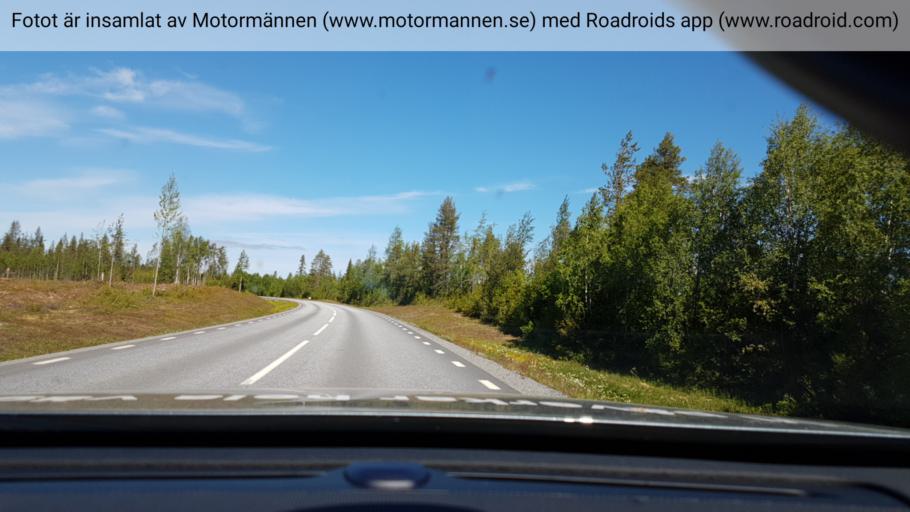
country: SE
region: Vaesterbotten
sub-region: Vilhelmina Kommun
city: Vilhelmina
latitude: 64.5032
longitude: 16.7751
